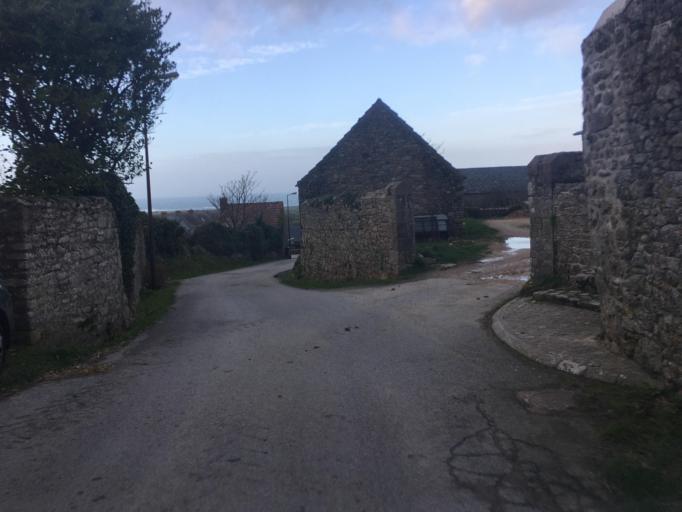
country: FR
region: Lower Normandy
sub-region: Departement de la Manche
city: Beaumont-Hague
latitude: 49.7117
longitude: -1.9220
